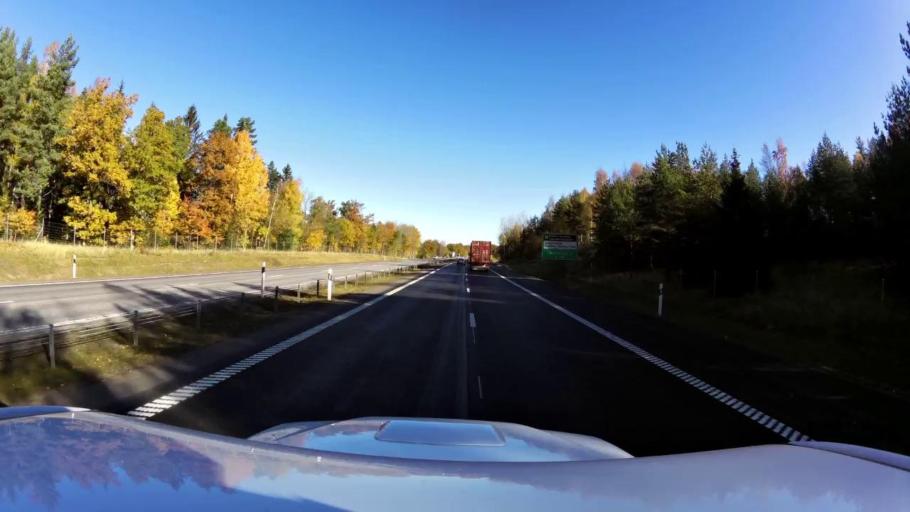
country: SE
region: OEstergoetland
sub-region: Linkopings Kommun
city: Malmslatt
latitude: 58.4242
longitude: 15.4936
